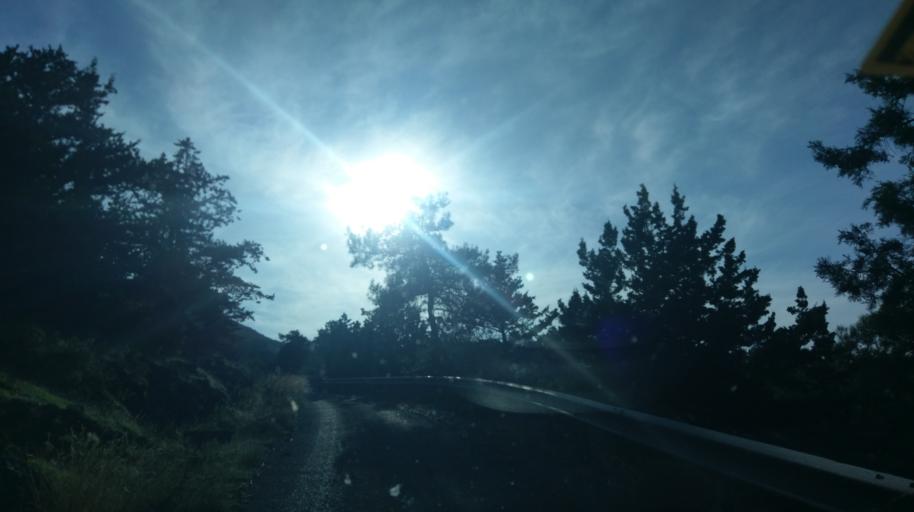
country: CY
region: Ammochostos
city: Lefkonoiko
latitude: 35.3319
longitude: 33.6343
